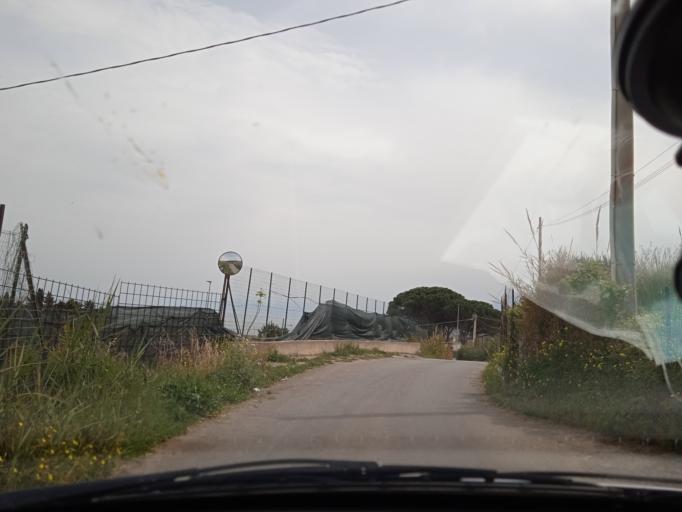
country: IT
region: Sicily
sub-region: Palermo
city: Altavilla Milicia
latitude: 38.0406
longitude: 13.5619
